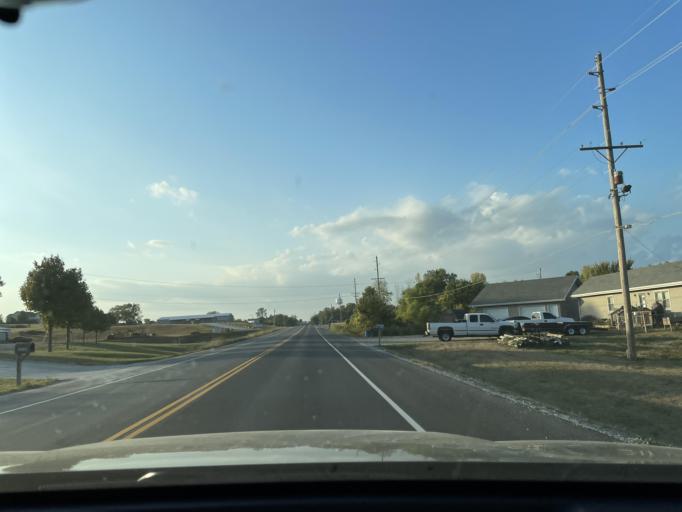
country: US
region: Missouri
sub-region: Andrew County
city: Country Club Village
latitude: 39.8236
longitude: -94.8518
